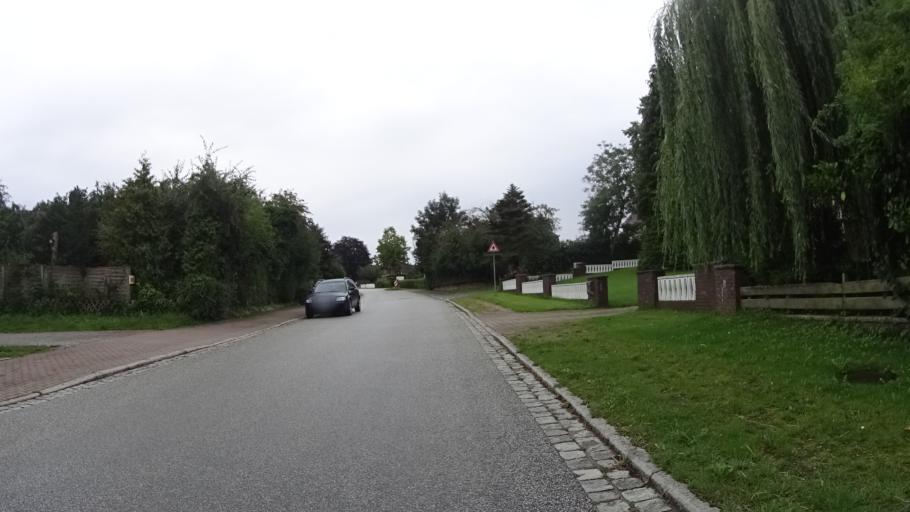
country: DE
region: Schleswig-Holstein
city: Stubben
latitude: 53.7218
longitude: 10.4041
